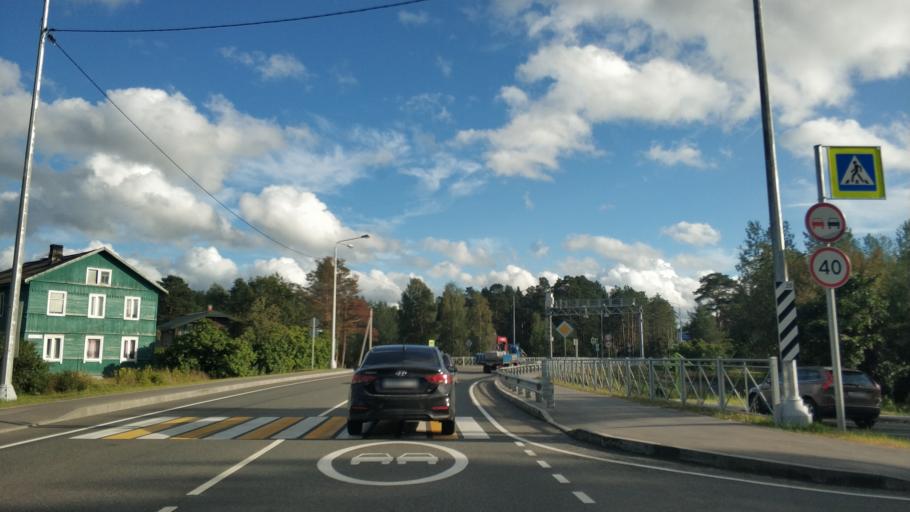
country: RU
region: Leningrad
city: Priozersk
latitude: 60.9996
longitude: 30.1825
